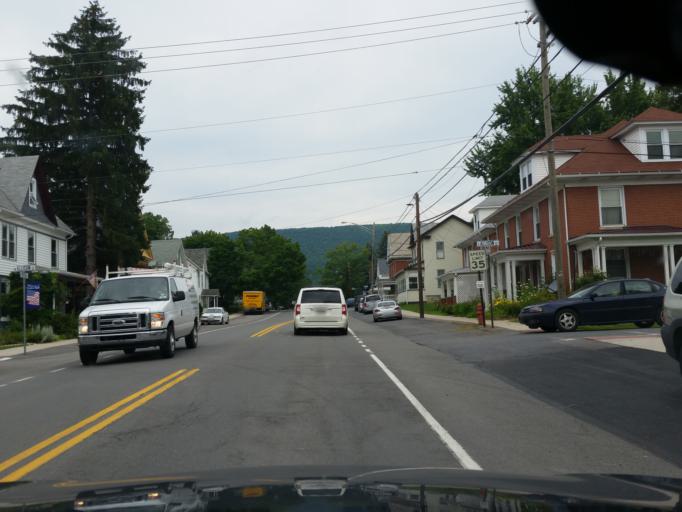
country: US
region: Pennsylvania
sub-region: Centre County
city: Centre Hall
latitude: 40.8405
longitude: -77.6787
